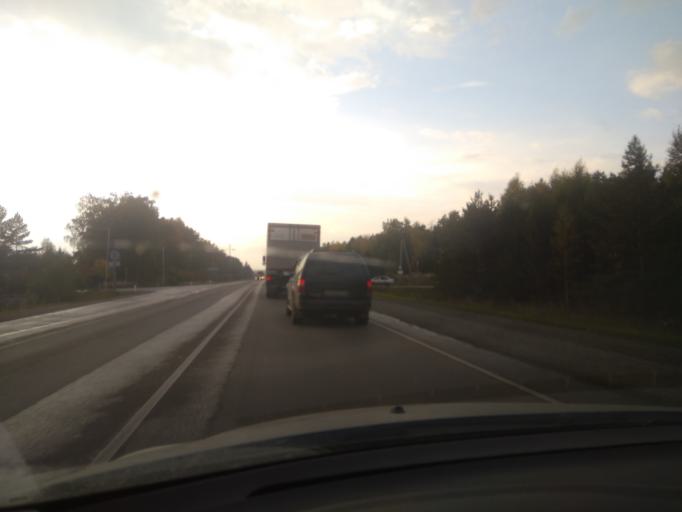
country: RU
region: Sverdlovsk
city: Verkhneye Dubrovo
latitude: 56.7224
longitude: 61.0469
